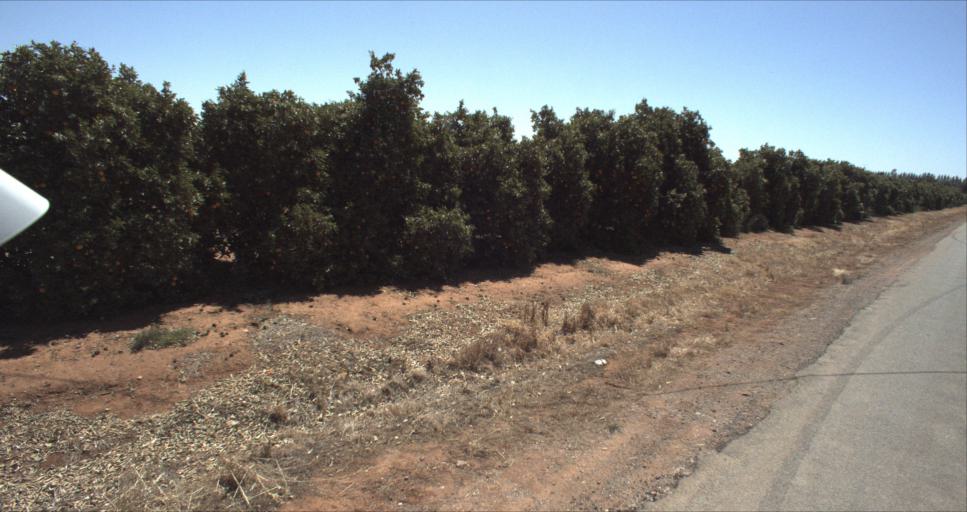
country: AU
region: New South Wales
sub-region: Leeton
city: Leeton
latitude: -34.5340
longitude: 146.3285
